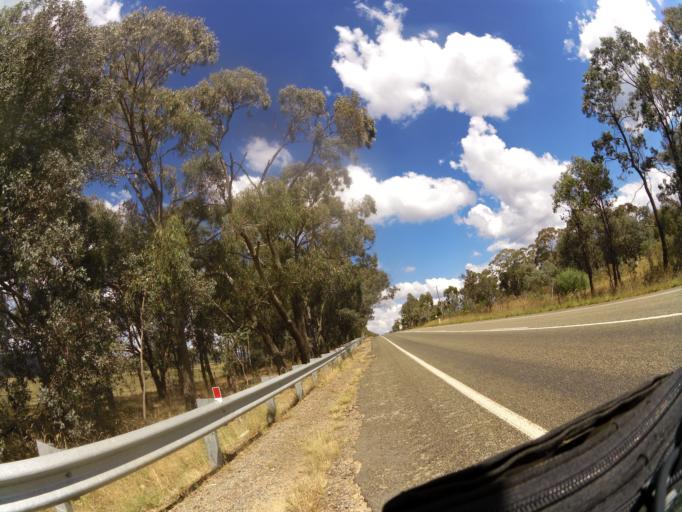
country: AU
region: Victoria
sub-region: Benalla
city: Benalla
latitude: -36.7903
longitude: 146.0108
